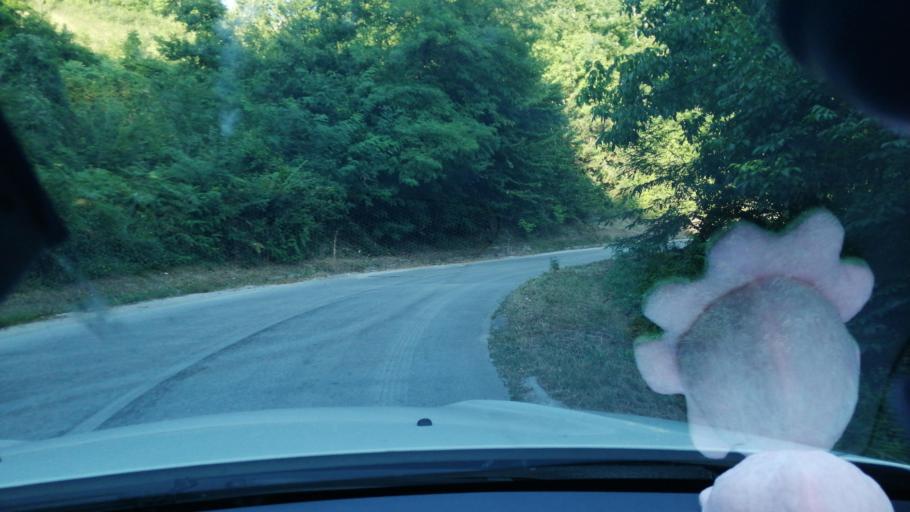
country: RS
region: Central Serbia
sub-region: Moravicki Okrug
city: Cacak
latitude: 43.8431
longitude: 20.2814
